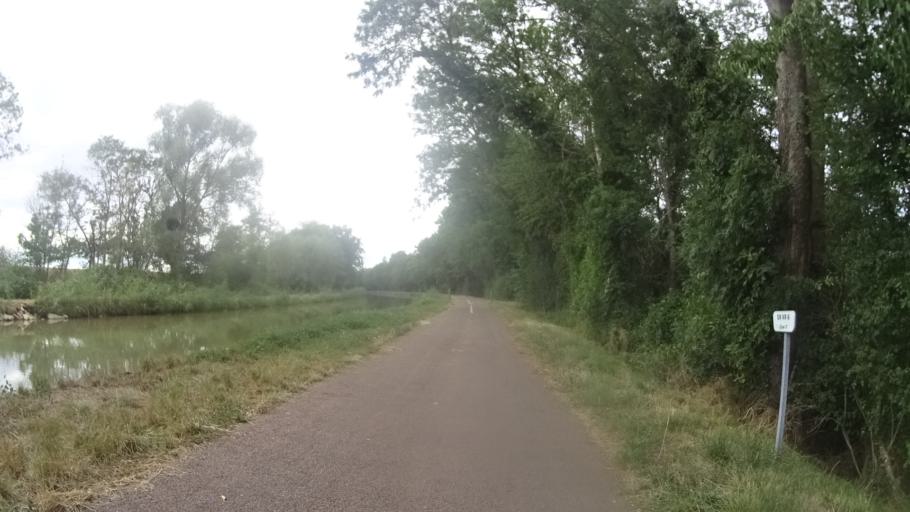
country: FR
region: Bourgogne
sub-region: Departement de la Nievre
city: Sermoise-sur-Loire
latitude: 46.9622
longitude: 3.1945
